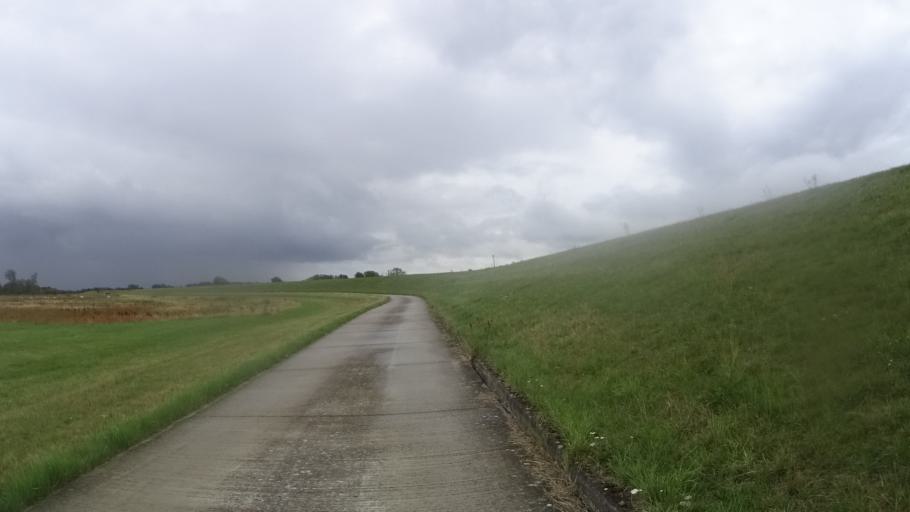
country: DE
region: Lower Saxony
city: Neu Darchau
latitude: 53.2574
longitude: 10.8503
